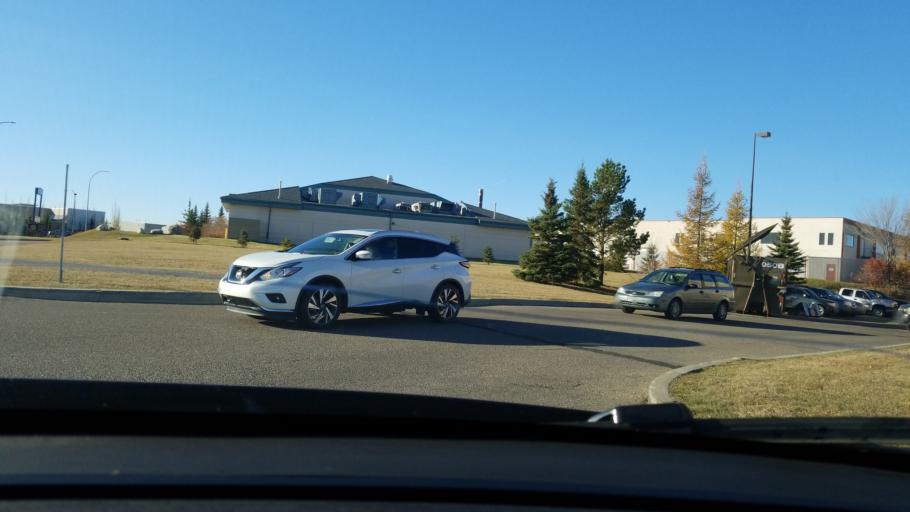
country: CA
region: Alberta
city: Sherwood Park
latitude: 53.5459
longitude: -113.3160
